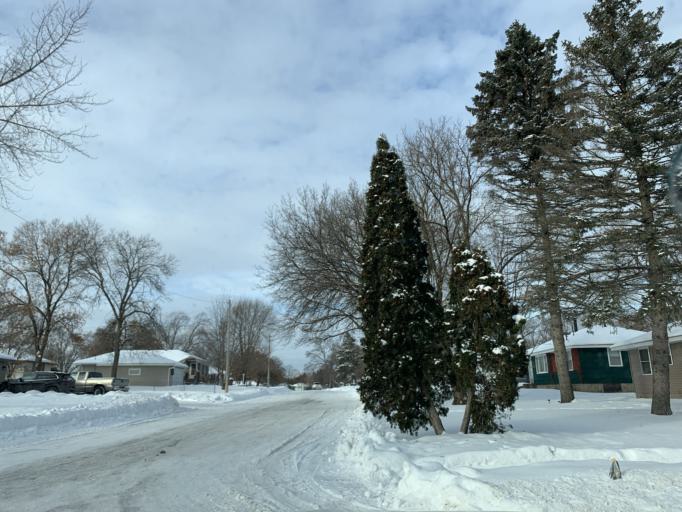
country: US
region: Minnesota
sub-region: Anoka County
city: Coon Rapids
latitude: 45.1705
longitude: -93.2858
